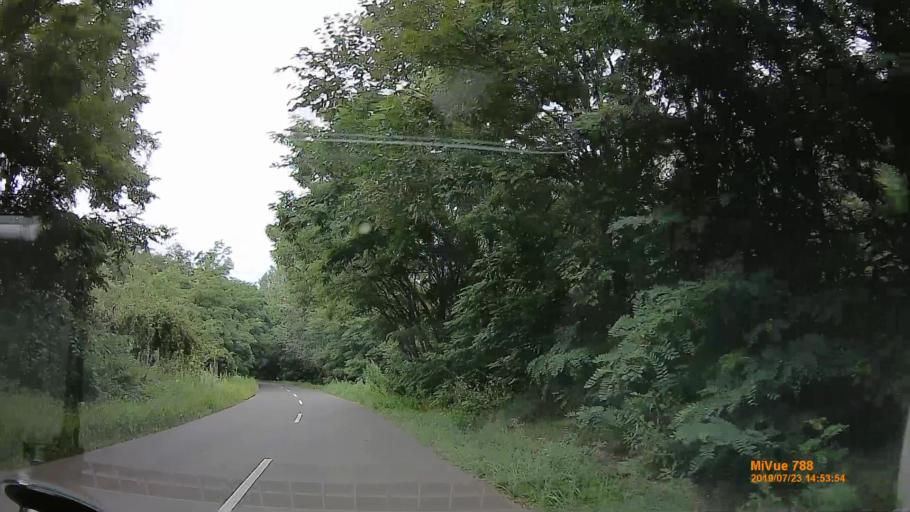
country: HU
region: Szabolcs-Szatmar-Bereg
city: Kalmanhaza
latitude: 47.8817
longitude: 21.6527
